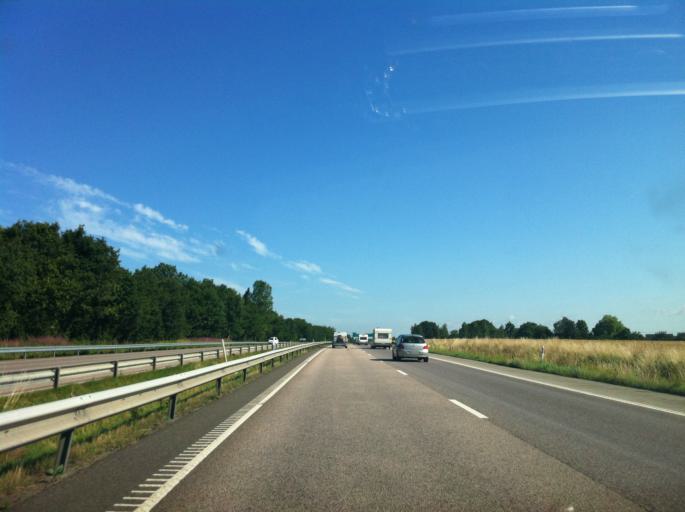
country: SE
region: Skane
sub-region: Helsingborg
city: Gantofta
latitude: 56.0048
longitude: 12.7799
